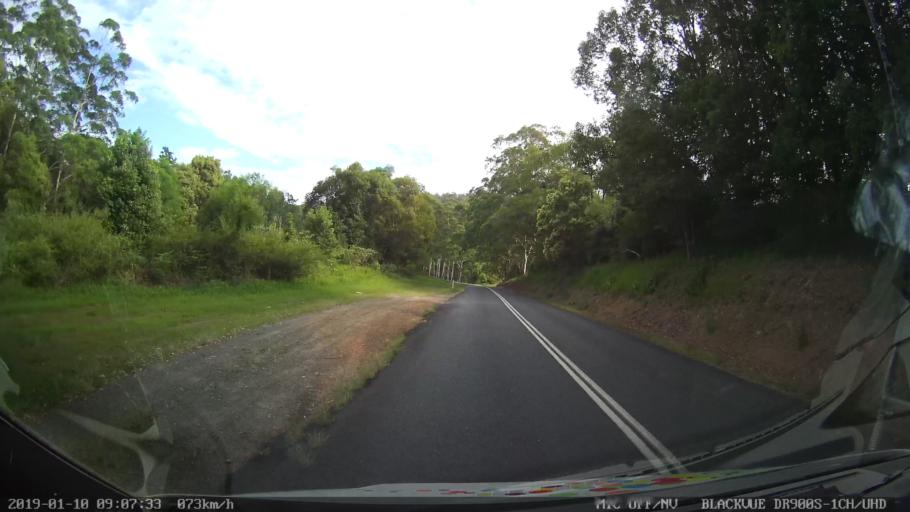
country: AU
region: New South Wales
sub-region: Coffs Harbour
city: Coffs Harbour
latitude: -30.2383
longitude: 153.0270
